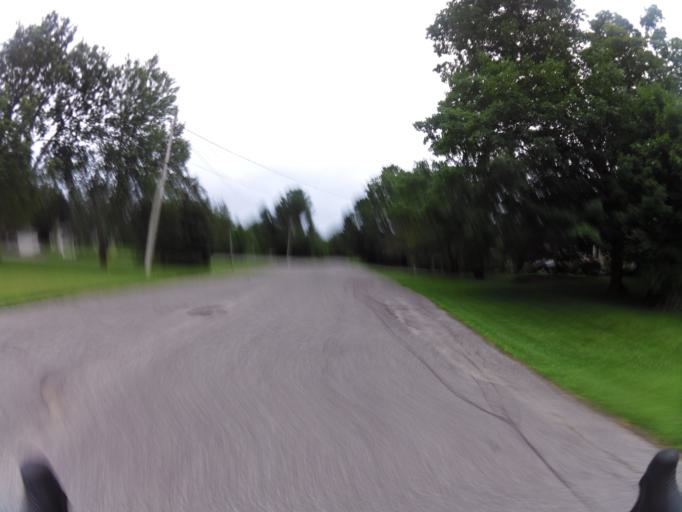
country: CA
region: Ontario
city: Ottawa
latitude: 45.3170
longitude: -75.7220
